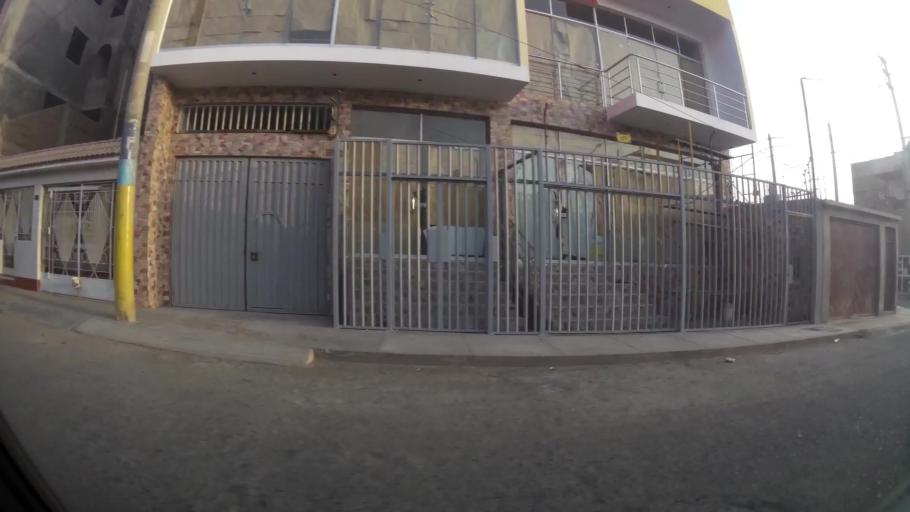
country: PE
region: Lima
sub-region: Huaura
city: Huacho
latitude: -11.1081
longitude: -77.6002
